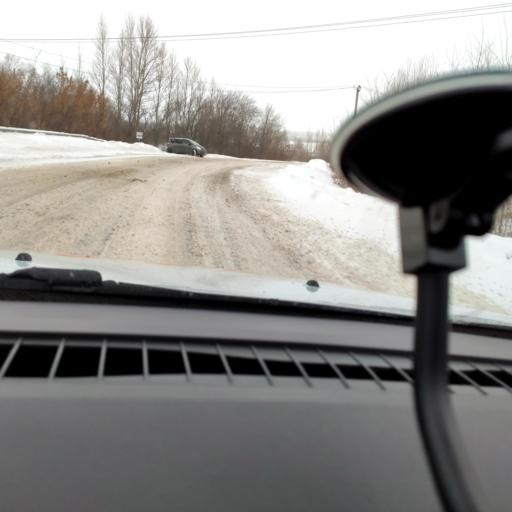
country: RU
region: Samara
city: Dubovyy Umet
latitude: 53.0392
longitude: 50.2318
